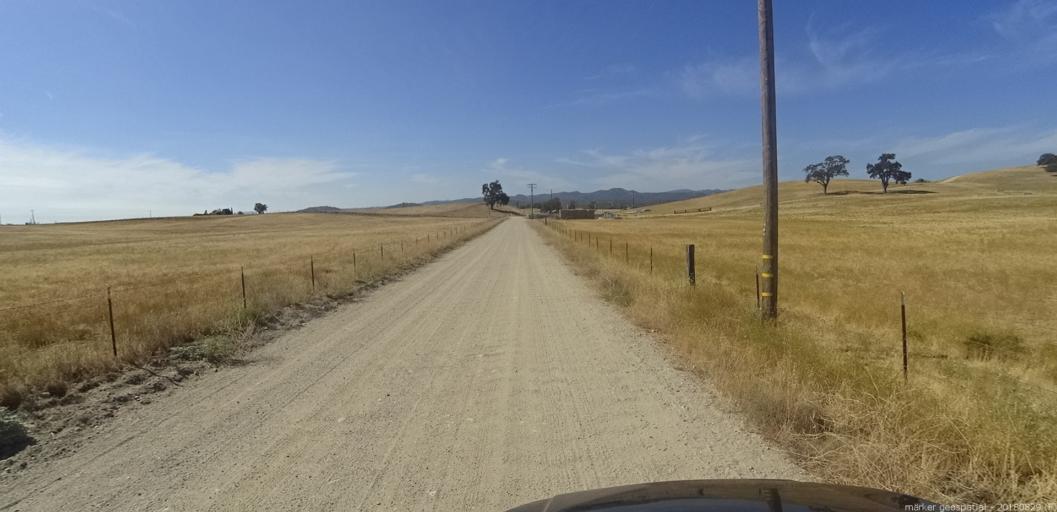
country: US
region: California
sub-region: Monterey County
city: King City
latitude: 35.9540
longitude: -121.0999
